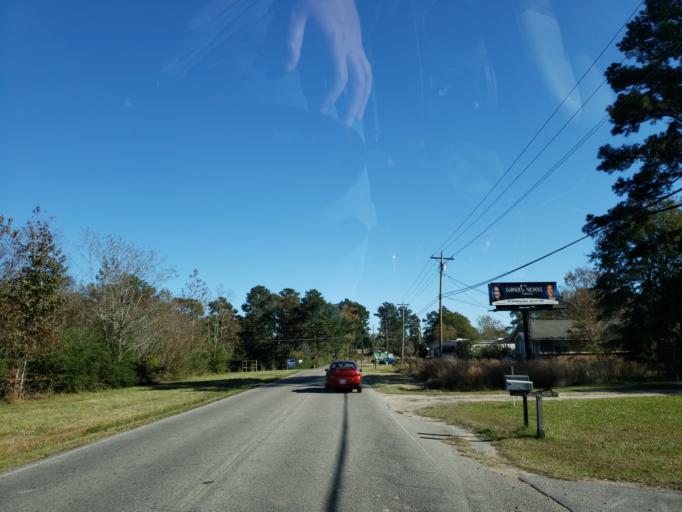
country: US
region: Mississippi
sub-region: Lamar County
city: West Hattiesburg
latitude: 31.3034
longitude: -89.3811
